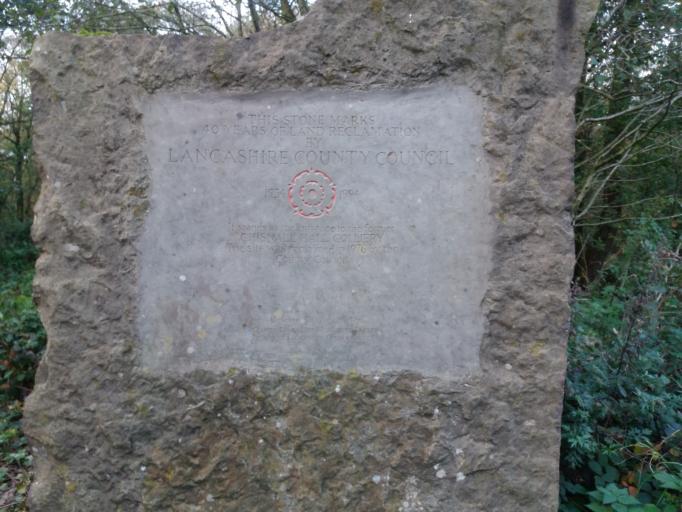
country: GB
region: England
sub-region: Lancashire
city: Coppull
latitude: 53.6088
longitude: -2.6752
